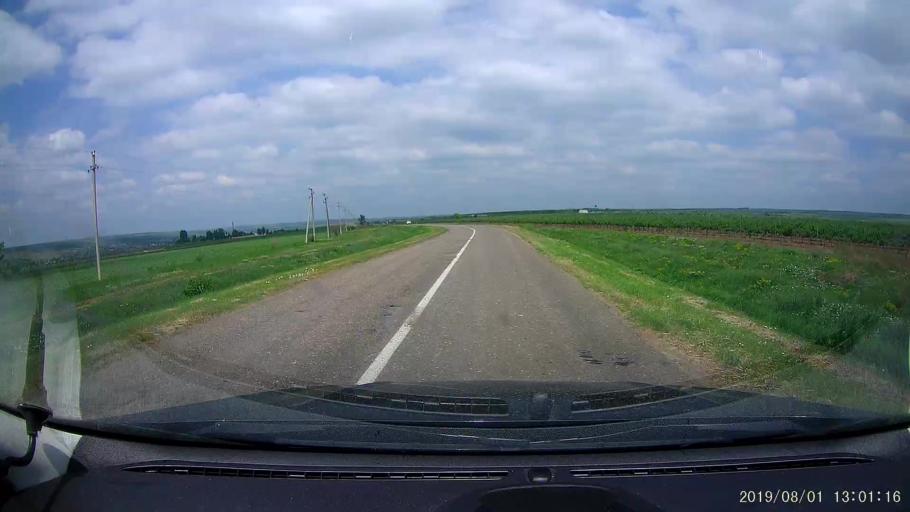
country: MD
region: Gagauzia
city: Vulcanesti
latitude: 45.7349
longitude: 28.3993
